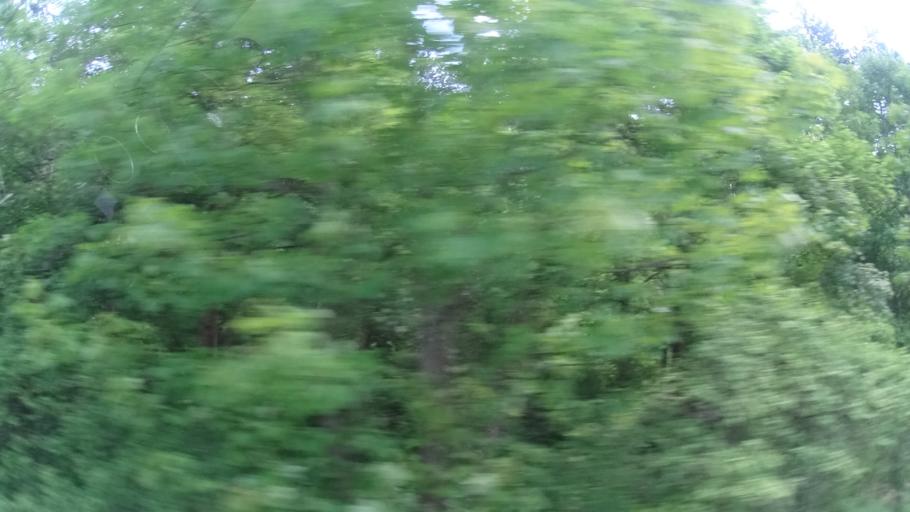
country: DE
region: Thuringia
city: Plaue
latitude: 50.8209
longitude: 10.9113
